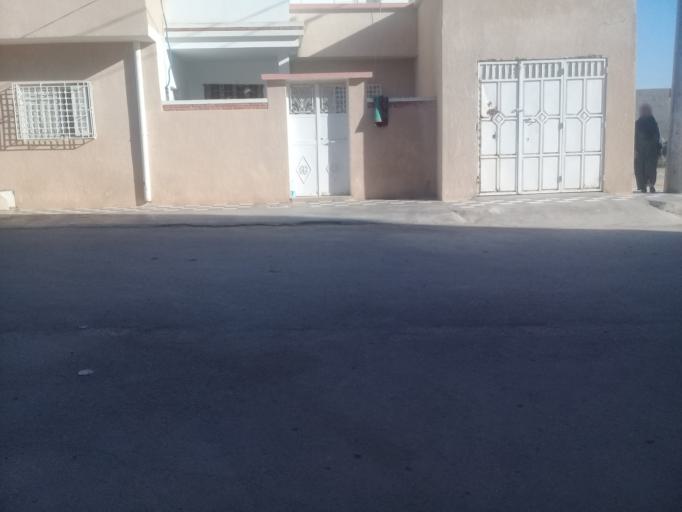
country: TN
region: Al Qayrawan
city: Kairouan
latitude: 35.6584
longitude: 10.1069
